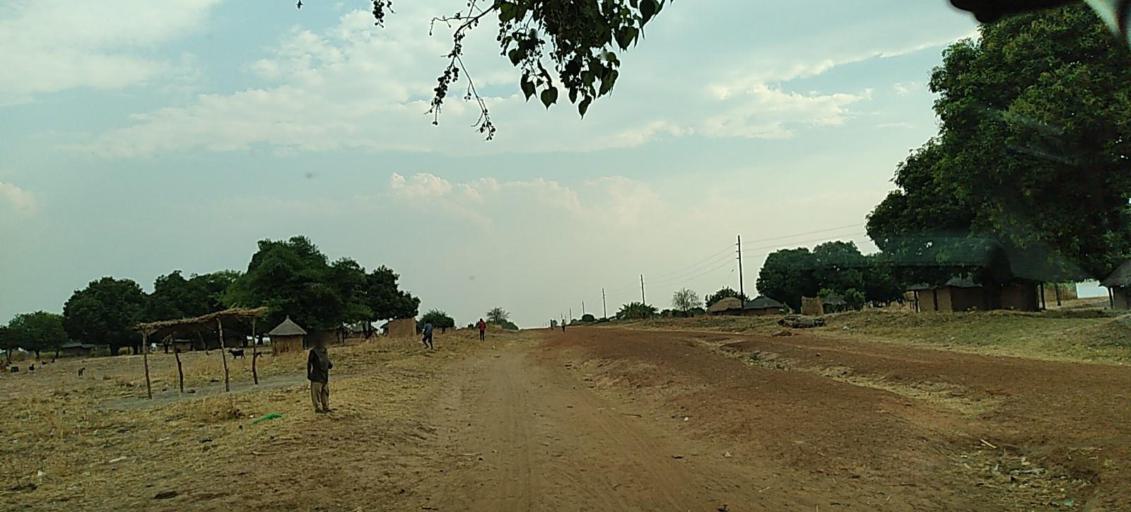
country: ZM
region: North-Western
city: Kabompo
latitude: -13.8676
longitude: 23.6694
